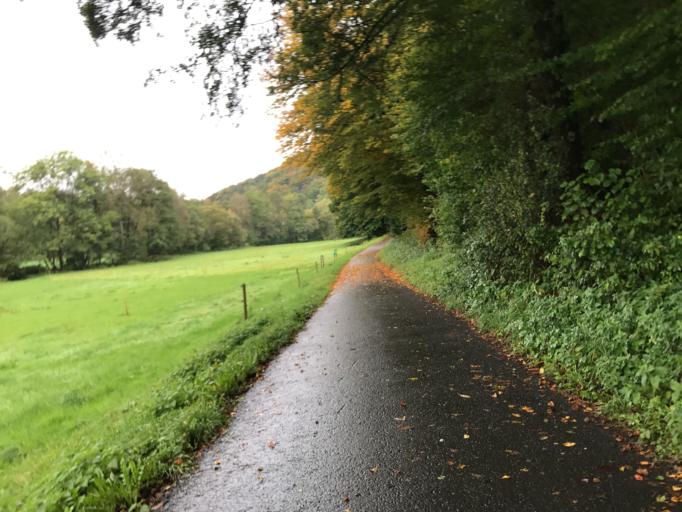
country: DE
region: Hesse
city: Witzenhausen
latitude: 51.3080
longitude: 9.8545
